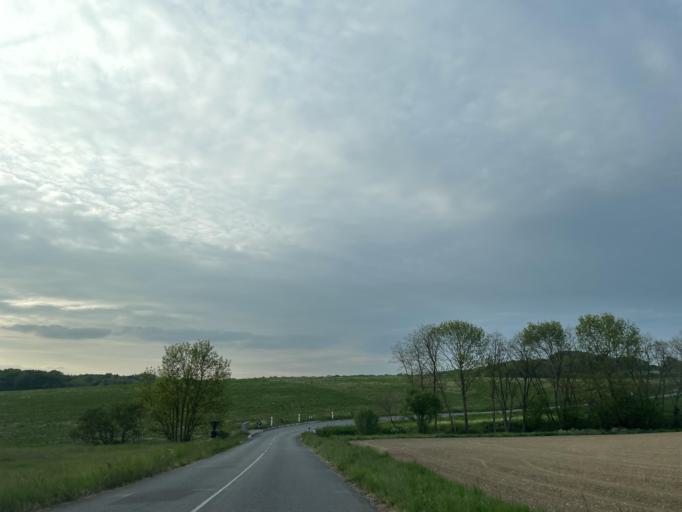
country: FR
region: Ile-de-France
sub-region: Departement de Seine-et-Marne
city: Bouleurs
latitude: 48.8974
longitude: 2.9071
